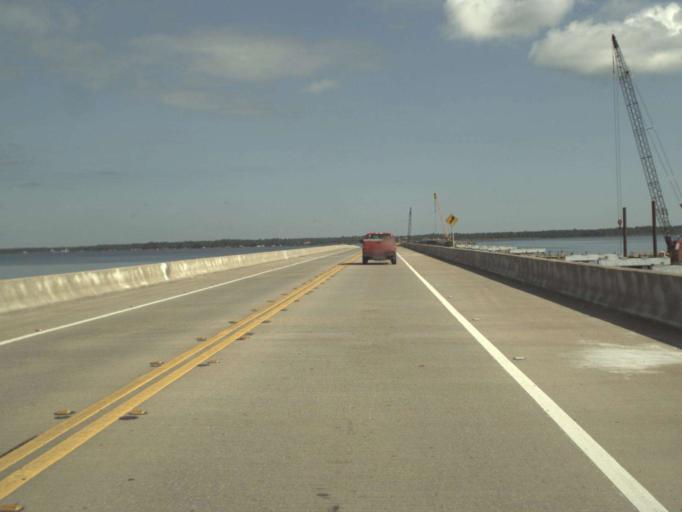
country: US
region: Florida
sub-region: Walton County
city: Seaside
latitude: 30.4103
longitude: -86.1640
